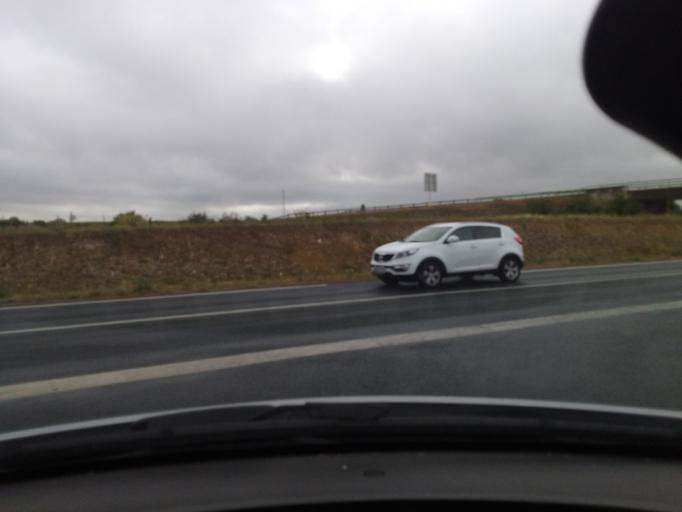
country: FR
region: Pays de la Loire
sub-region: Departement de la Vendee
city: Lucon
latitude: 46.4686
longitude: -1.1545
